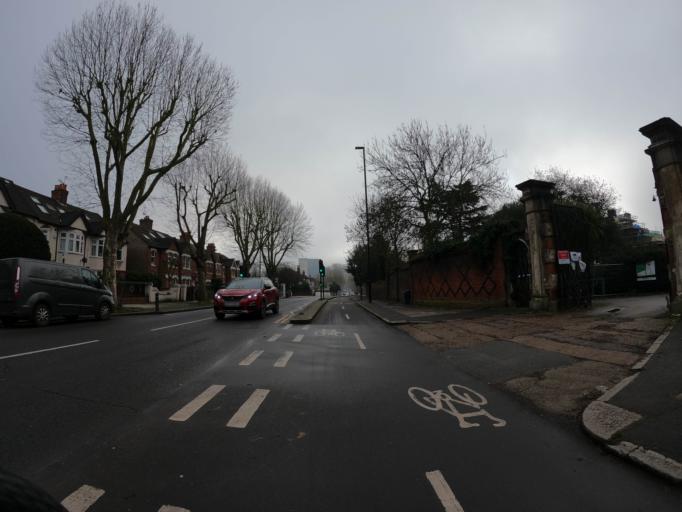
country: GB
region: England
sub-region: Greater London
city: Brentford
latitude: 51.4926
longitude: -0.3181
